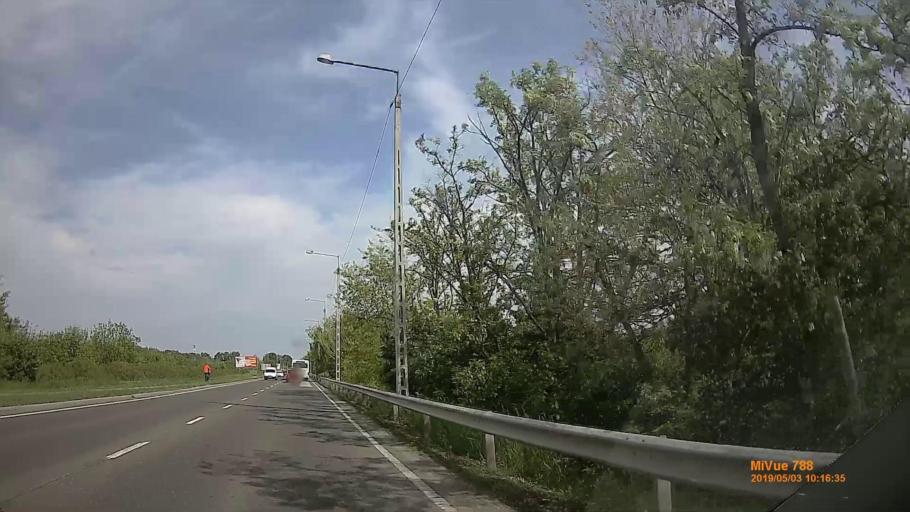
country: HU
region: Jasz-Nagykun-Szolnok
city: Szolnok
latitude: 47.1576
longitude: 20.2034
